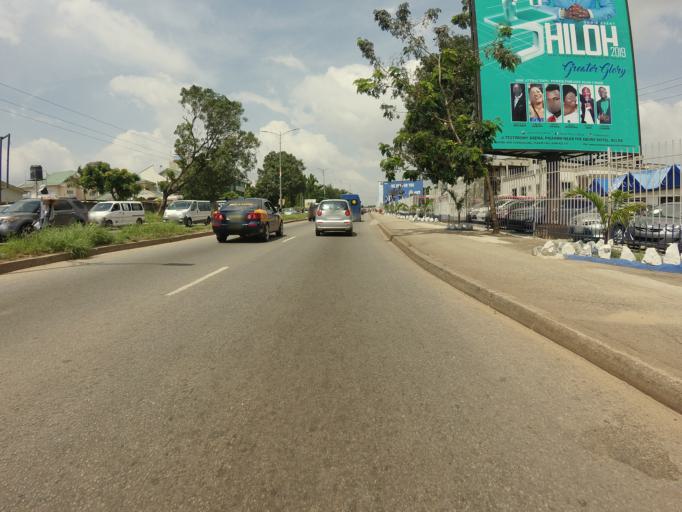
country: GH
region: Greater Accra
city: Dome
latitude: 5.6105
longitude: -0.2115
